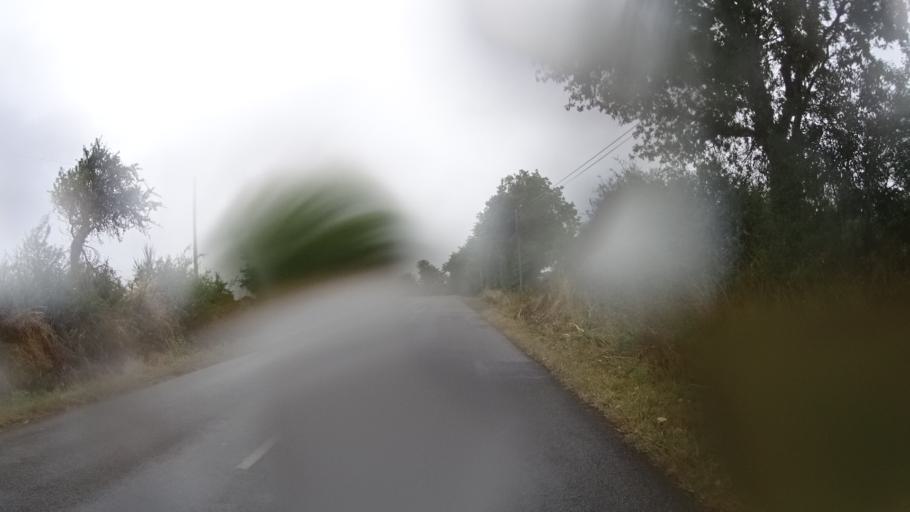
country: FR
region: Pays de la Loire
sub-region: Departement de la Loire-Atlantique
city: Corsept
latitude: 47.2693
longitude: -2.0901
